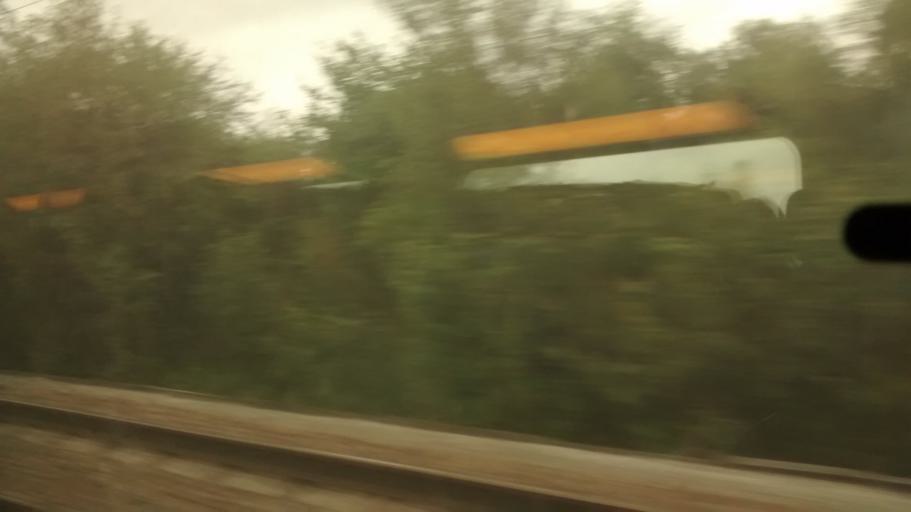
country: FR
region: Bourgogne
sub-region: Departement de l'Yonne
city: Tanlay
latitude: 47.7702
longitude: 4.0258
